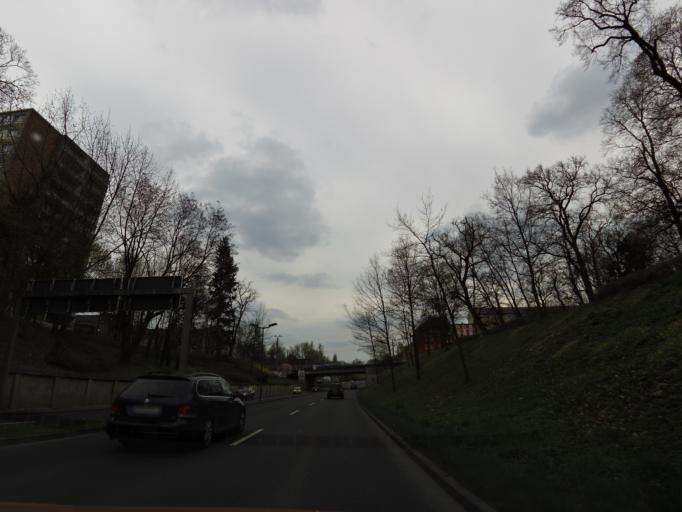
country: DE
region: Brandenburg
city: Frankfurt (Oder)
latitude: 52.3441
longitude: 14.5401
